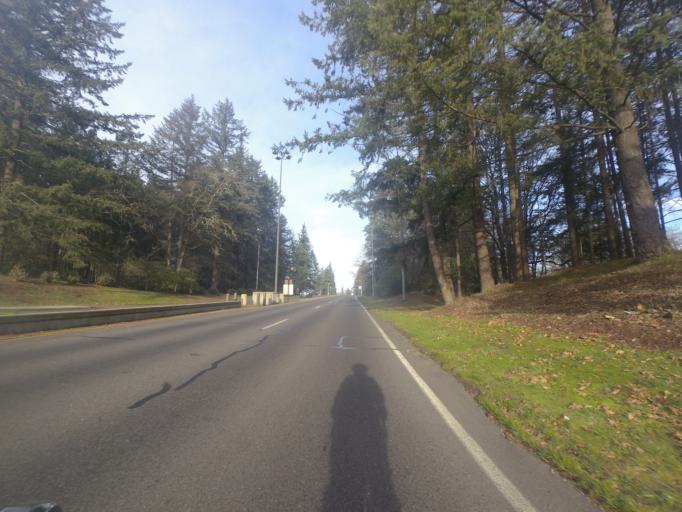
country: US
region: Washington
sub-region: Pierce County
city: McChord Air Force Base
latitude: 47.1377
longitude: -122.5008
